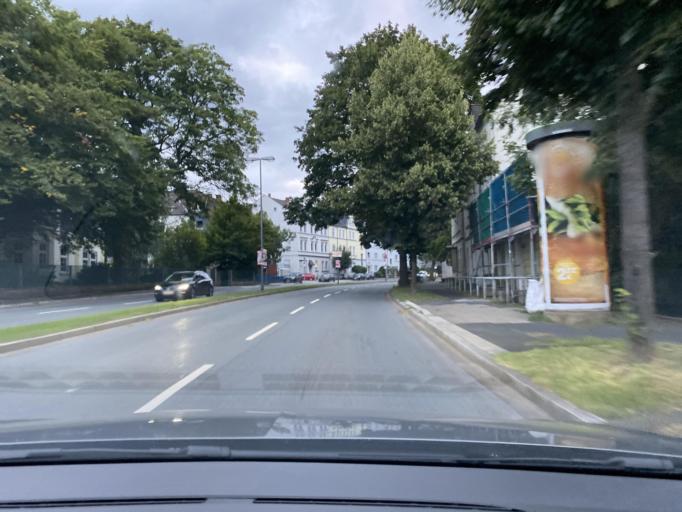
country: DE
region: North Rhine-Westphalia
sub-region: Regierungsbezirk Munster
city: Gelsenkirchen
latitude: 51.4476
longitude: 7.0926
